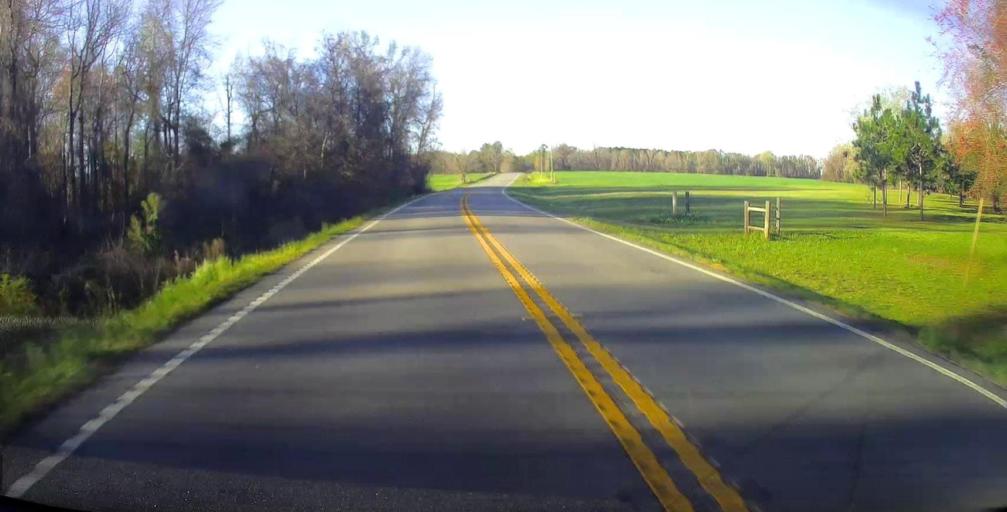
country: US
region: Georgia
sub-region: Pulaski County
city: Hawkinsville
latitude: 32.1718
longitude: -83.3616
